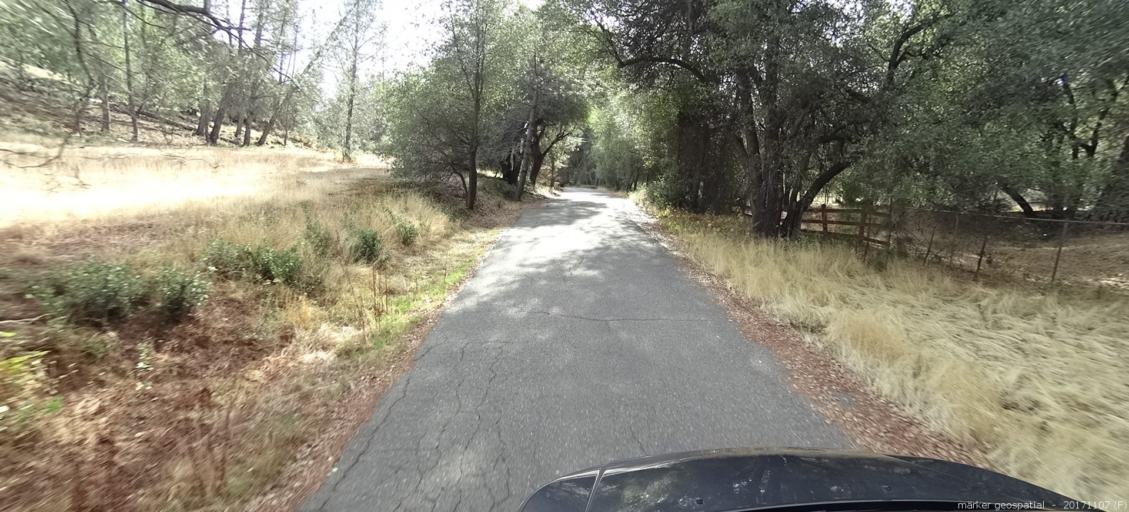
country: US
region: California
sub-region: Shasta County
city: Shasta
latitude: 40.5383
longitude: -122.5269
